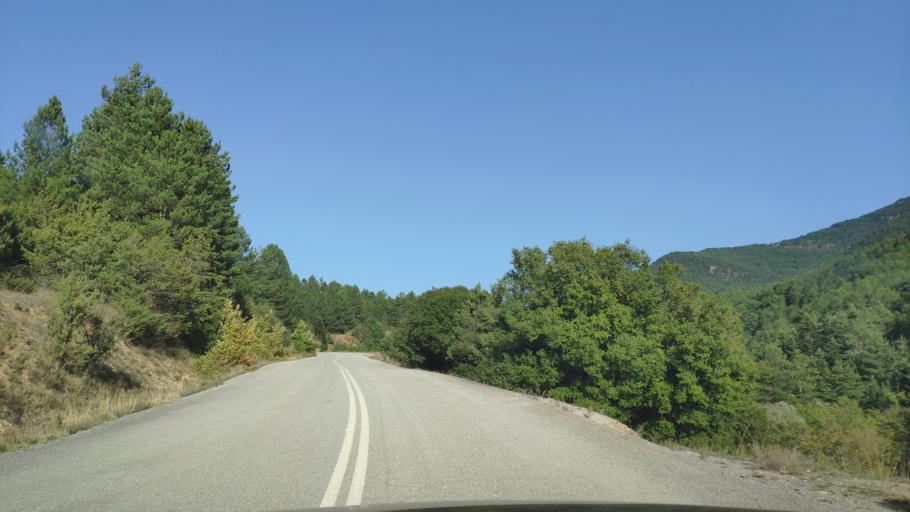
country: GR
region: West Greece
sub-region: Nomos Achaias
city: Aiyira
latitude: 37.9927
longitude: 22.3683
